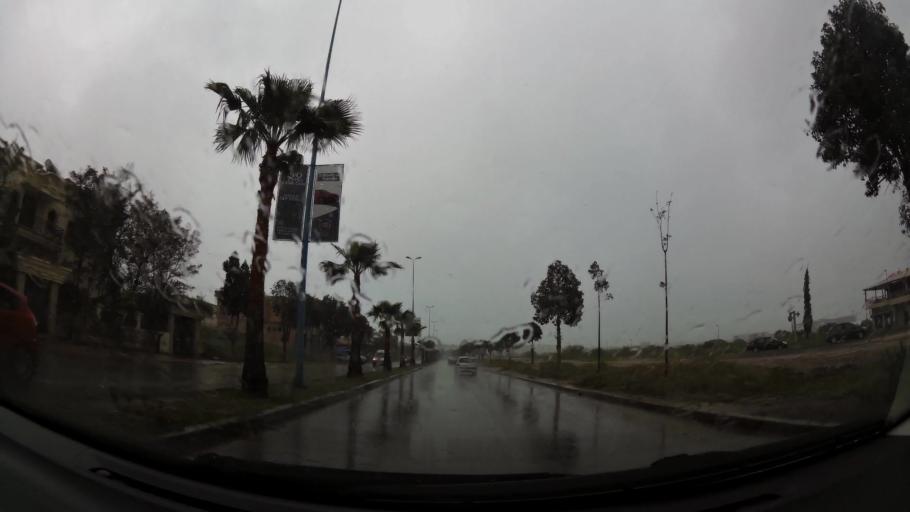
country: MA
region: Grand Casablanca
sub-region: Casablanca
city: Casablanca
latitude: 33.5439
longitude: -7.6645
